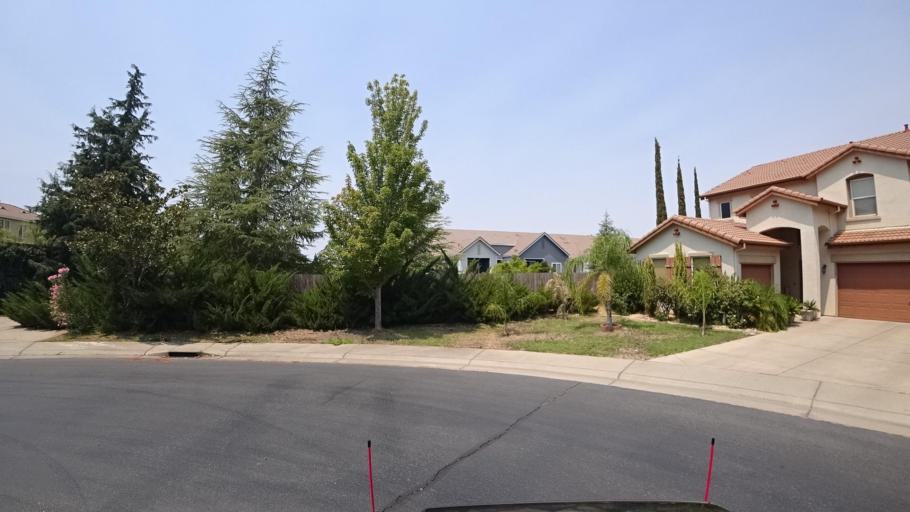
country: US
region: California
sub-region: Placer County
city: Roseville
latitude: 38.7958
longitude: -121.2840
